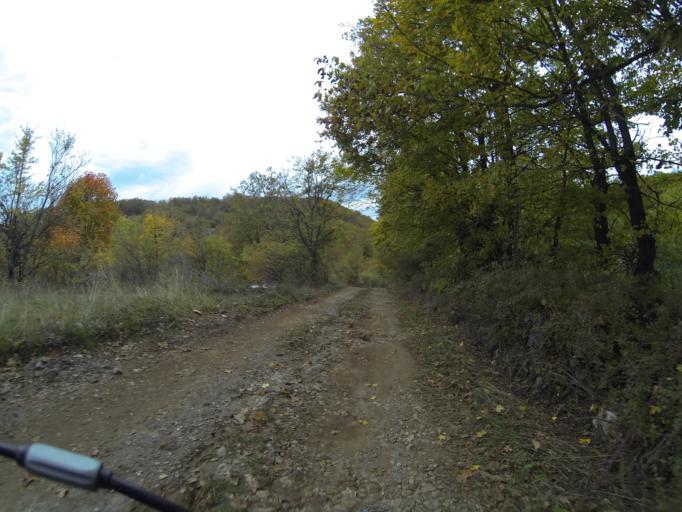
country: RO
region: Gorj
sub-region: Comuna Tismana
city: Sohodol
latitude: 45.0766
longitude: 22.8583
